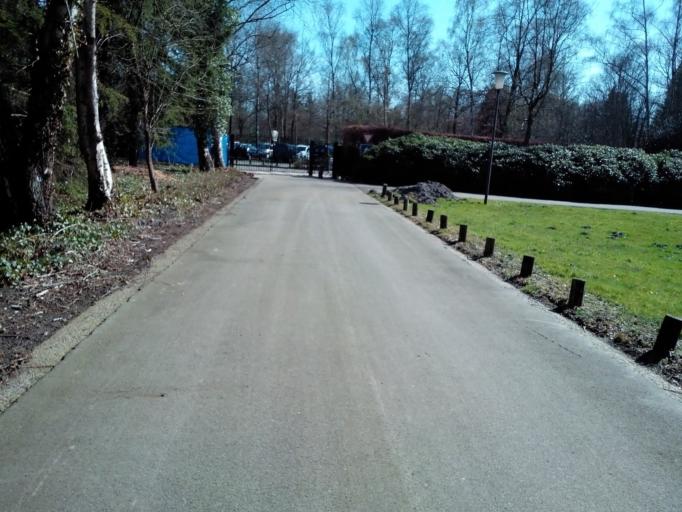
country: BE
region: Flanders
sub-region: Provincie Limburg
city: Zonhoven
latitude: 50.9591
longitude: 5.4045
